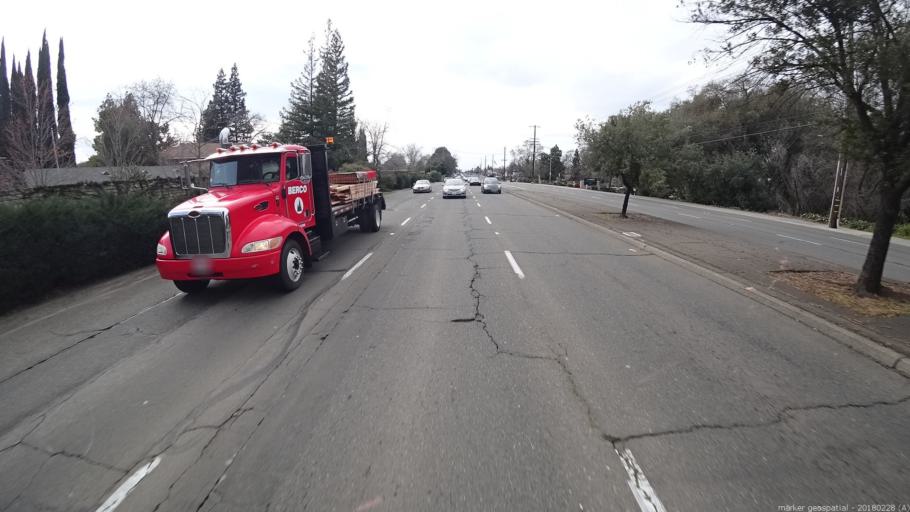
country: US
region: California
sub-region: Sacramento County
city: Fair Oaks
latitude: 38.6636
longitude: -121.2870
